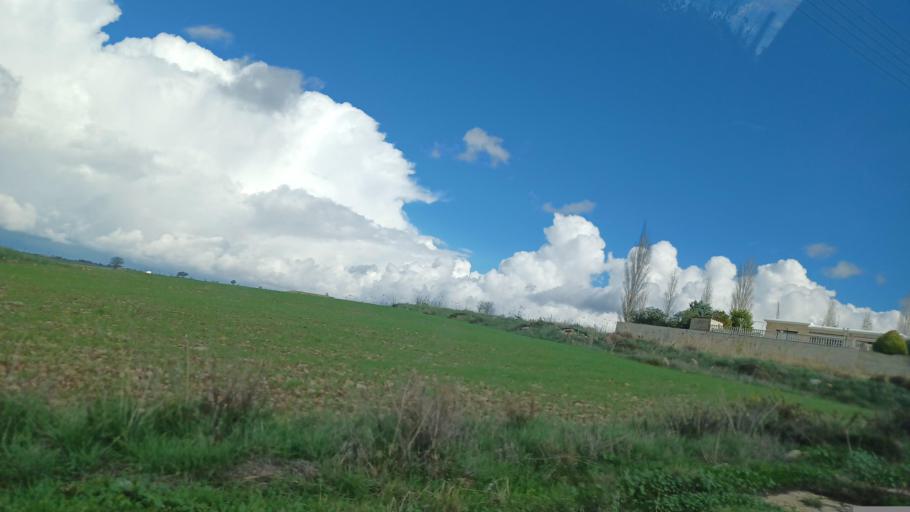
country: CY
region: Pafos
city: Pegeia
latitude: 34.9137
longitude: 32.4151
